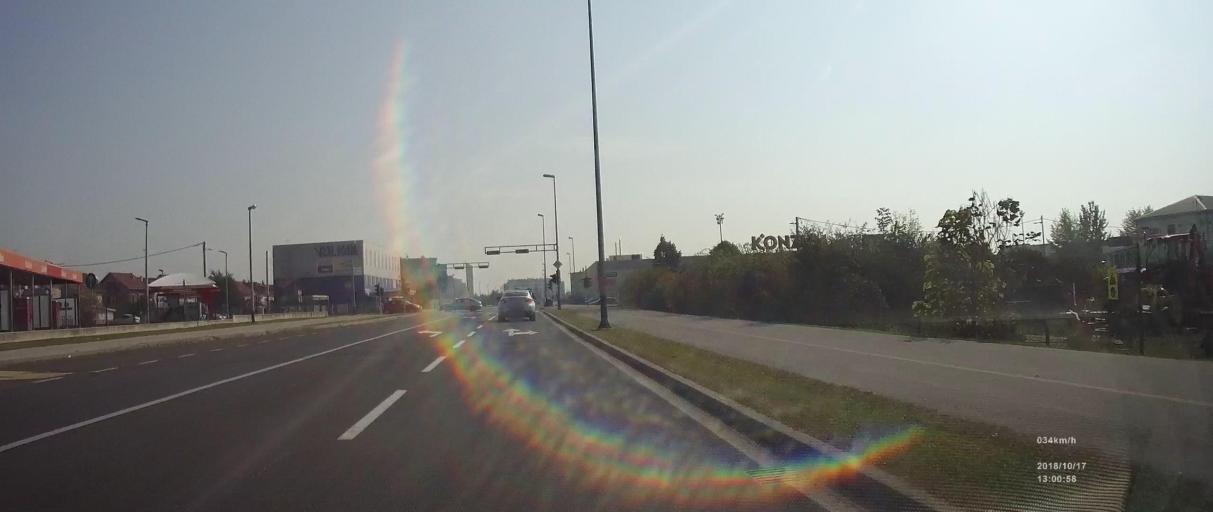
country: HR
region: Zagrebacka
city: Gradici
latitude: 45.7130
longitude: 16.0580
